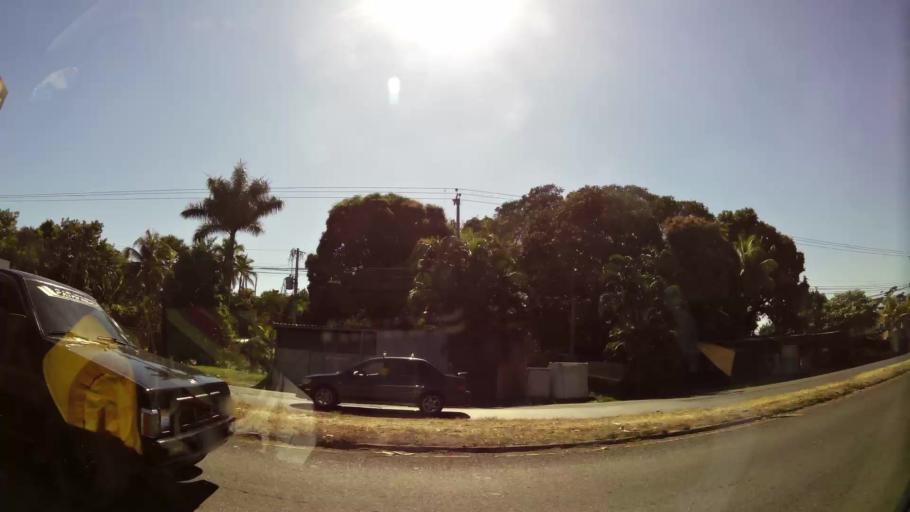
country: SV
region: La Libertad
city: Santa Tecla
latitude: 13.7269
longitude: -89.3763
